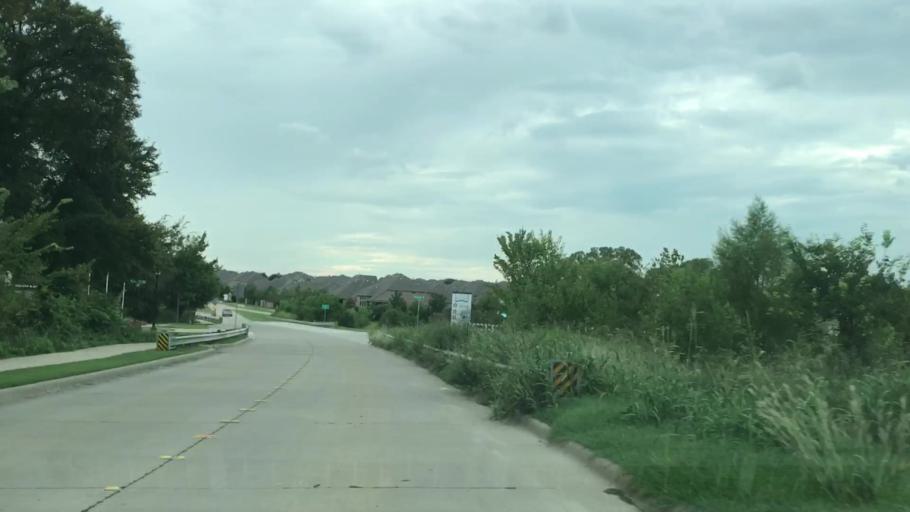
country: US
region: Texas
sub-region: Collin County
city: Prosper
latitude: 33.1890
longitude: -96.7882
